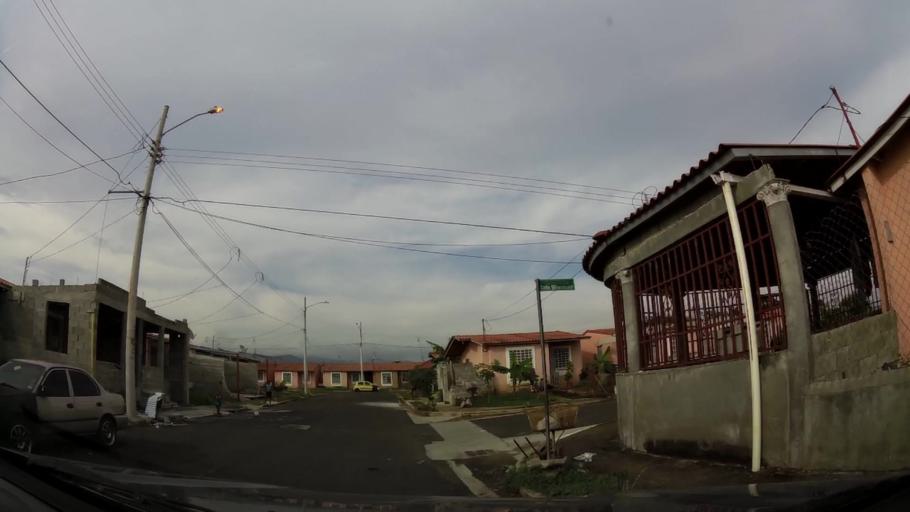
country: PA
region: Panama
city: Tocumen
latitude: 9.0696
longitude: -79.3610
